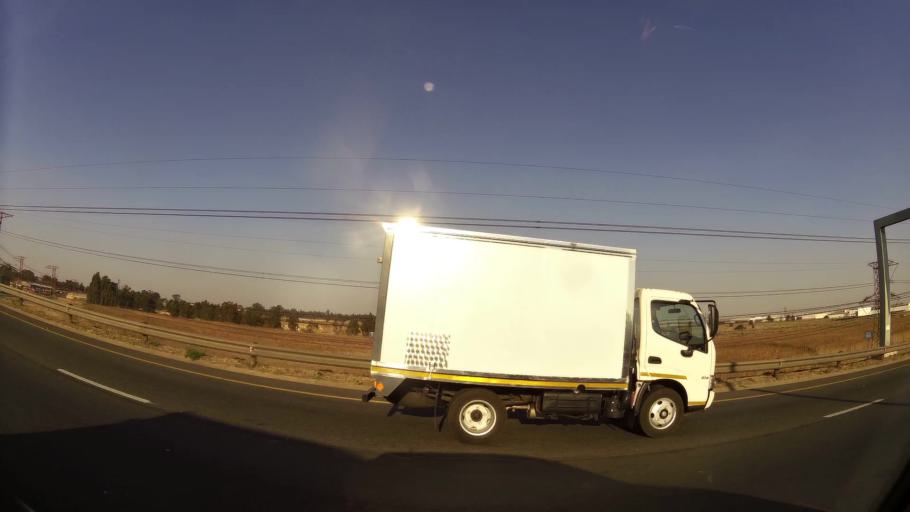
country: ZA
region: Gauteng
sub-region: Ekurhuleni Metropolitan Municipality
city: Germiston
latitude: -26.2195
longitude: 28.1296
